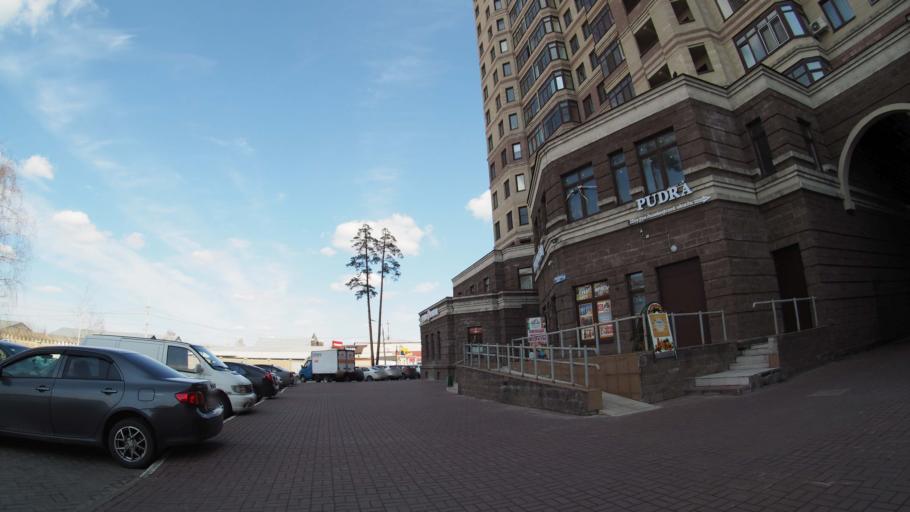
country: RU
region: Moskovskaya
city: Ramenskoye
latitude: 55.5812
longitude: 38.2130
